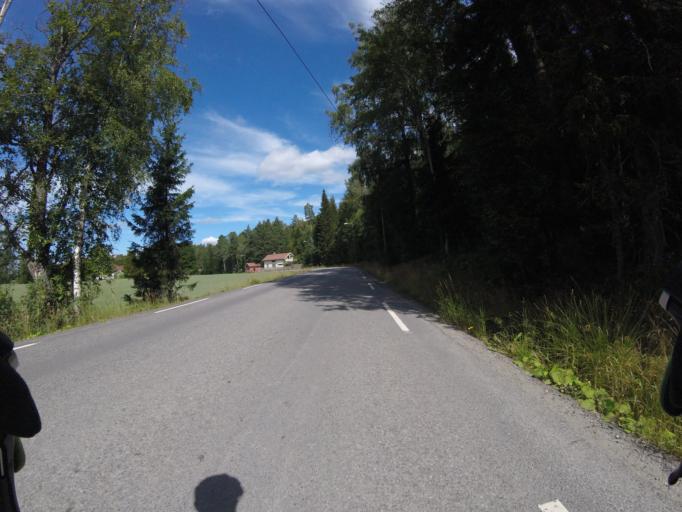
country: NO
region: Akershus
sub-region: Lorenskog
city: Kjenn
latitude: 59.8980
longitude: 10.9690
